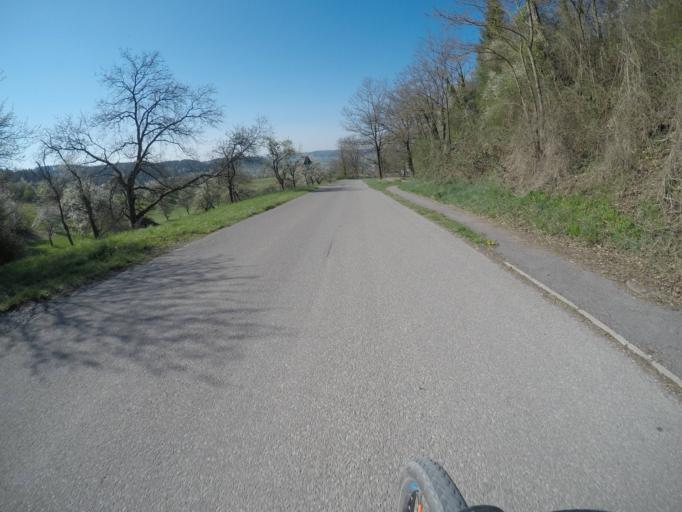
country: DE
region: Baden-Wuerttemberg
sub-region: Regierungsbezirk Stuttgart
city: Hildrizhausen
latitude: 48.5603
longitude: 8.9798
